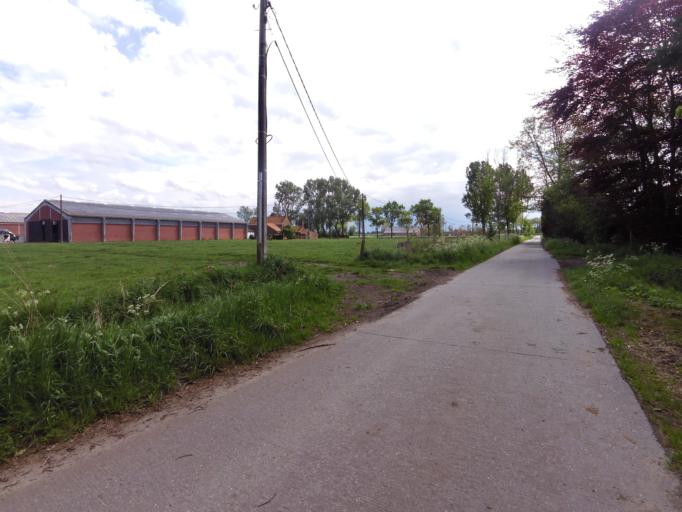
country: BE
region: Flanders
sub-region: Provincie West-Vlaanderen
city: Gistel
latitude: 51.1407
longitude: 2.9919
